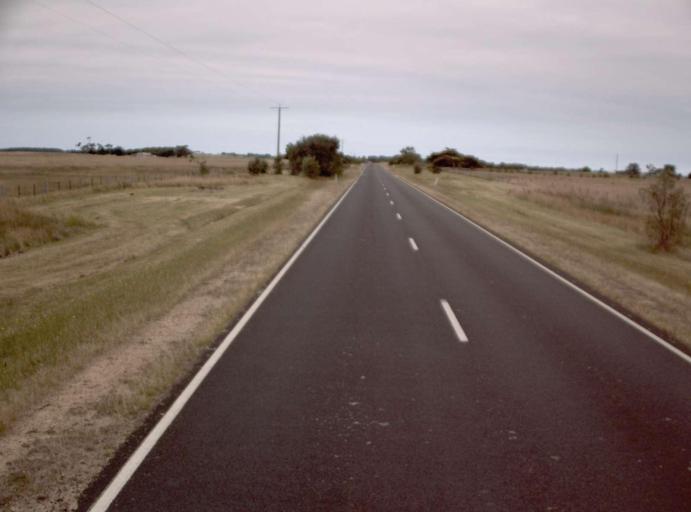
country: AU
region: Victoria
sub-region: Wellington
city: Sale
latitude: -38.5444
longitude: 146.9484
